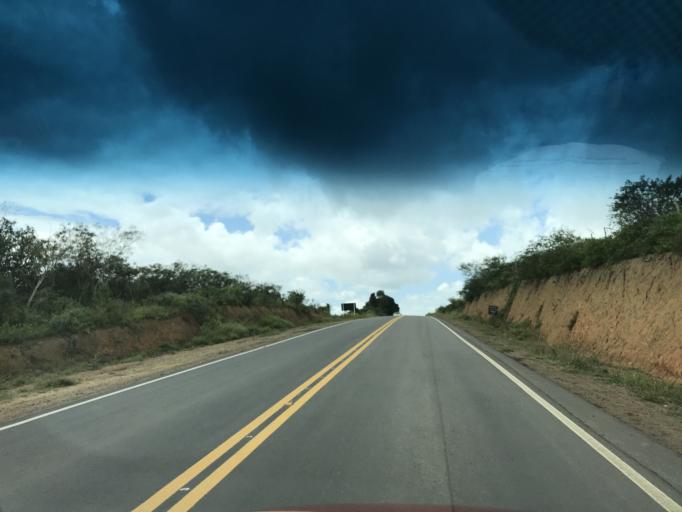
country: BR
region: Bahia
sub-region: Conceicao Do Almeida
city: Conceicao do Almeida
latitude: -12.7120
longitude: -39.2278
